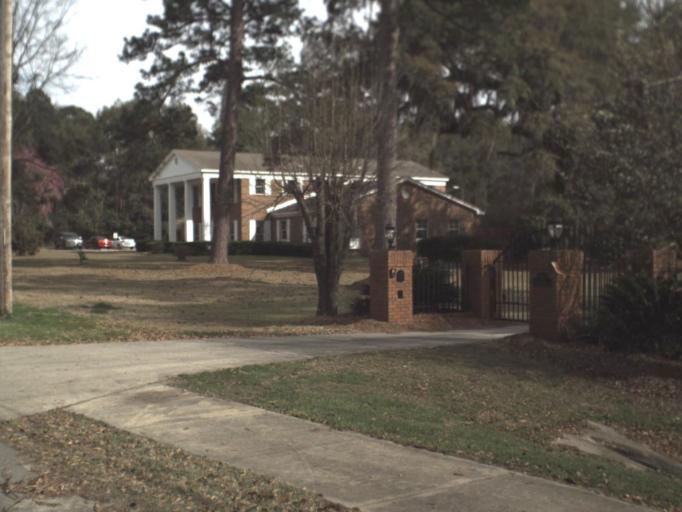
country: US
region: Florida
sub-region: Jefferson County
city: Monticello
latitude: 30.5451
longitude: -83.8791
